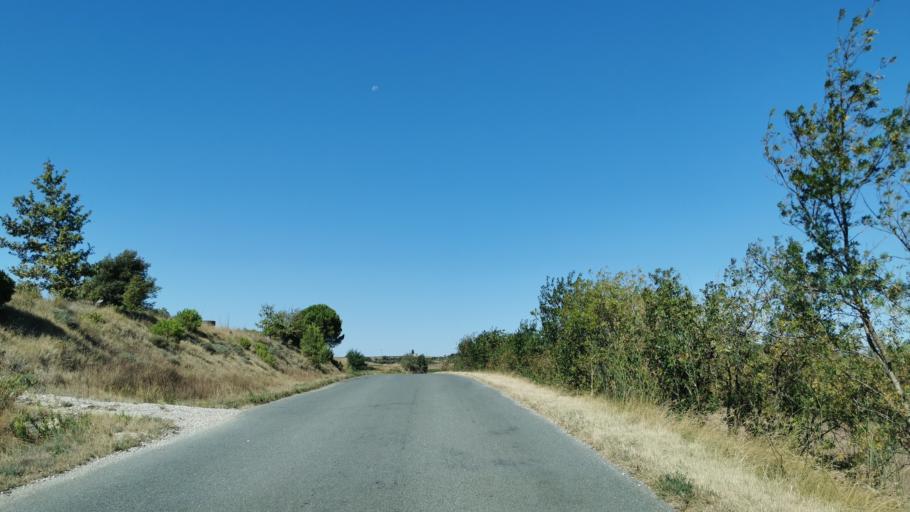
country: FR
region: Languedoc-Roussillon
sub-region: Departement de l'Aude
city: Conques-sur-Orbiel
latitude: 43.2528
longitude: 2.4320
